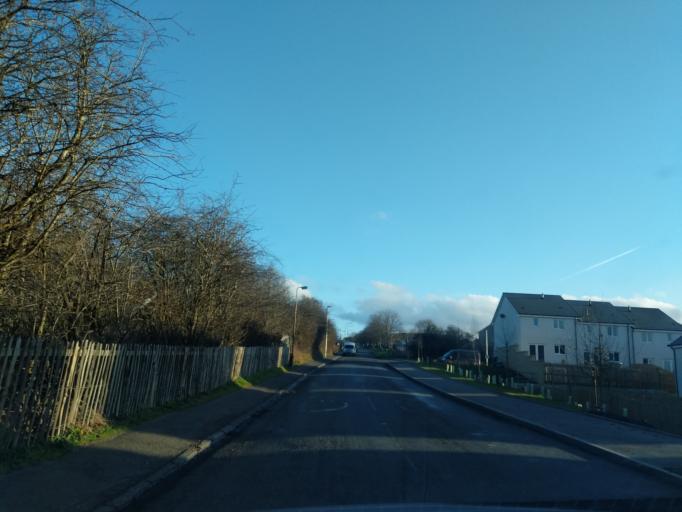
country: GB
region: Scotland
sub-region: Edinburgh
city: Currie
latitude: 55.9007
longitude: -3.3165
